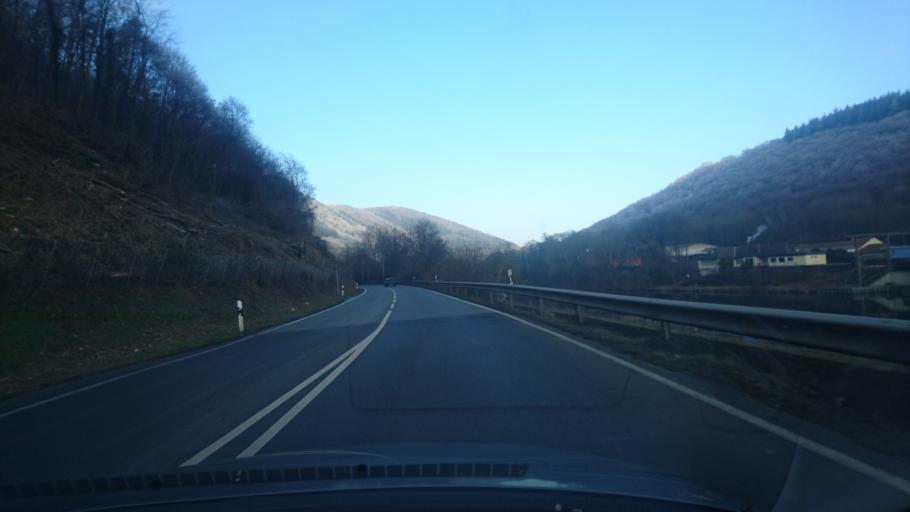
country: DE
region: Rheinland-Pfalz
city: Miellen
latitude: 50.3117
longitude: 7.6471
